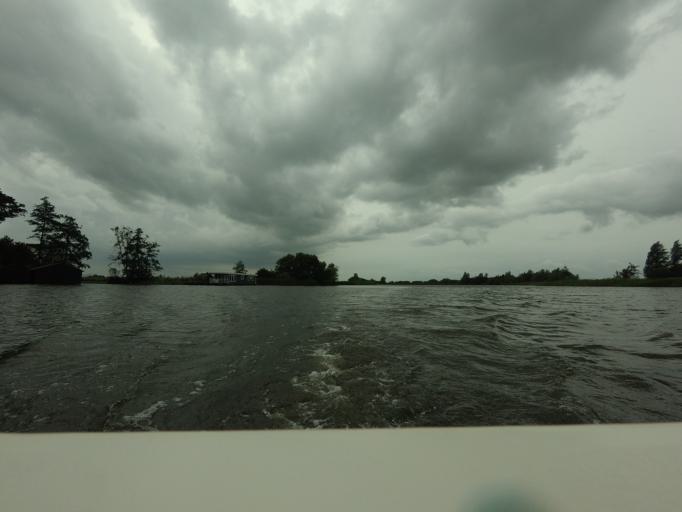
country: NL
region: Friesland
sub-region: Gemeente Smallingerland
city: Oudega
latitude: 53.0978
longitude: 5.9439
